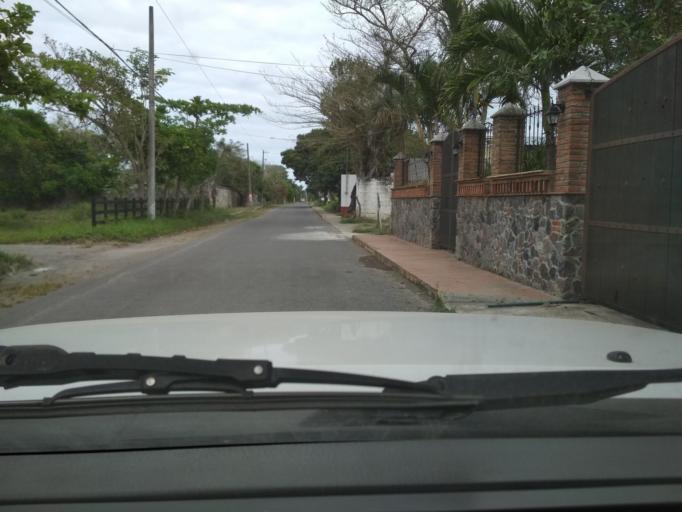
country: MX
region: Veracruz
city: El Tejar
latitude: 19.0737
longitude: -96.1437
